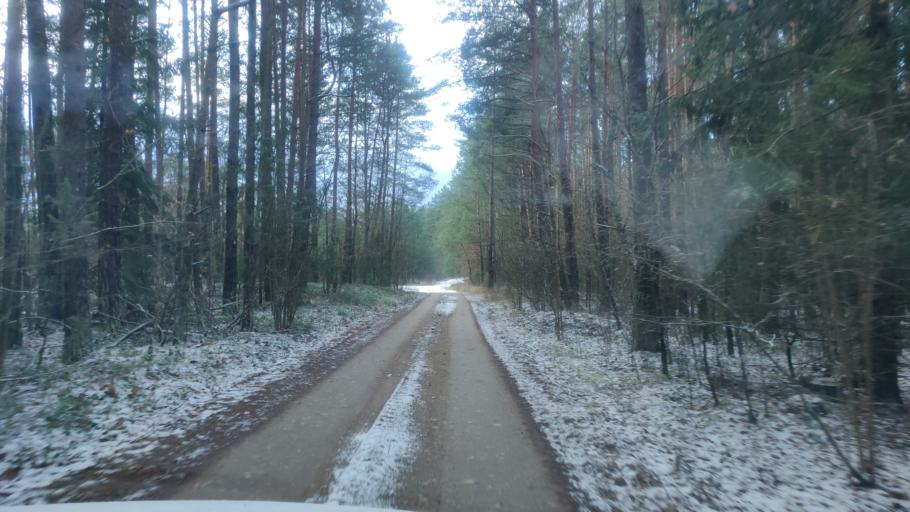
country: LT
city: Trakai
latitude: 54.5633
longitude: 24.9154
